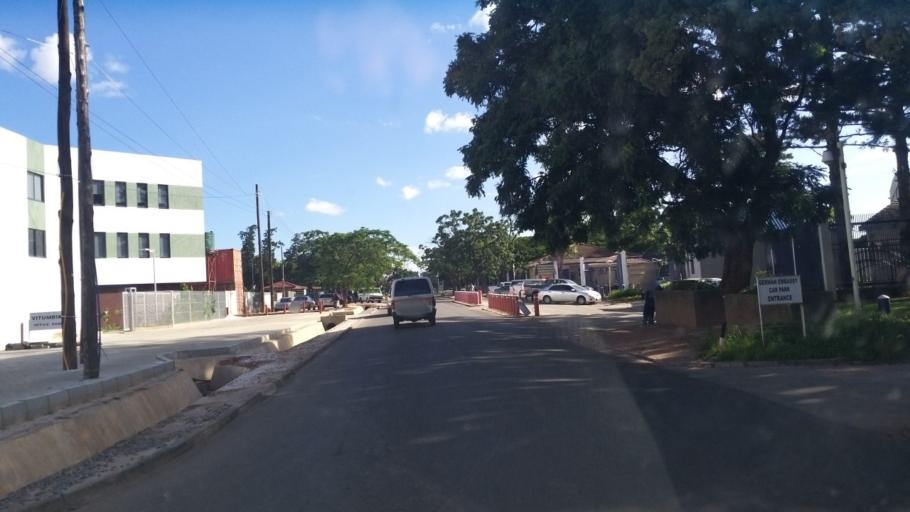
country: ZM
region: Lusaka
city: Lusaka
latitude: -15.4230
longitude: 28.3121
